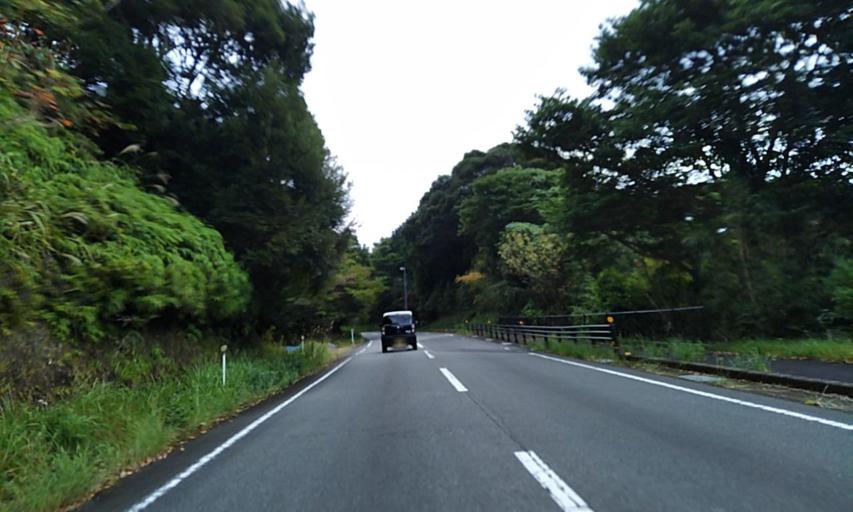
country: JP
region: Wakayama
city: Shingu
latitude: 33.4676
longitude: 135.8265
